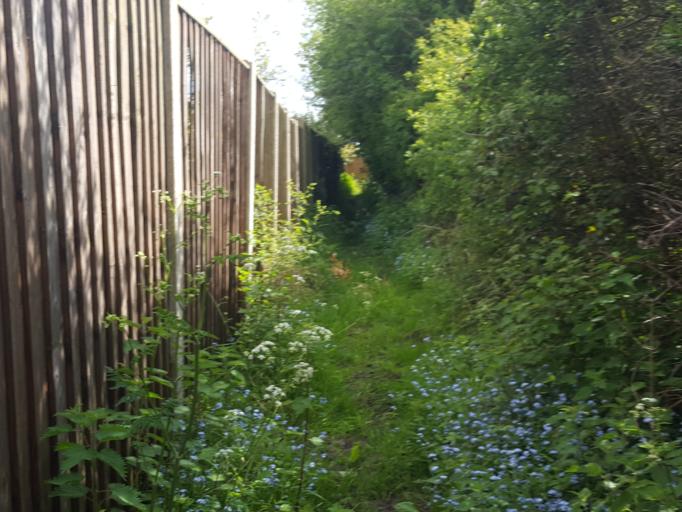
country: GB
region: England
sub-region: Essex
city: Frinton-on-Sea
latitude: 51.8347
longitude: 1.2082
